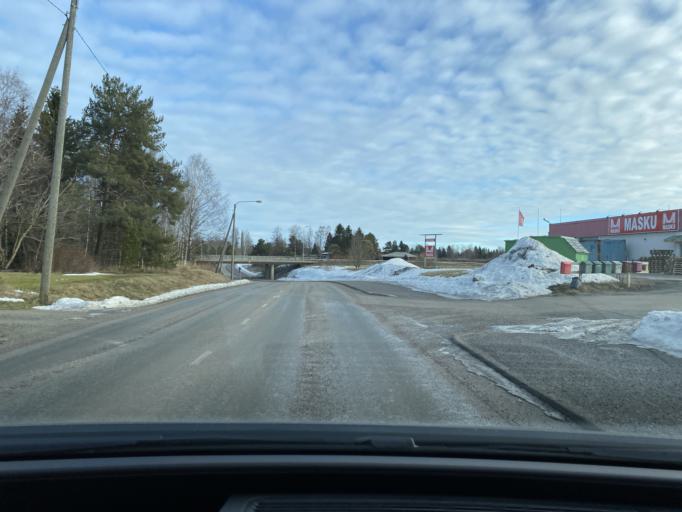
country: FI
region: Satakunta
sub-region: Pori
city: Huittinen
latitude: 61.1670
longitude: 22.6891
